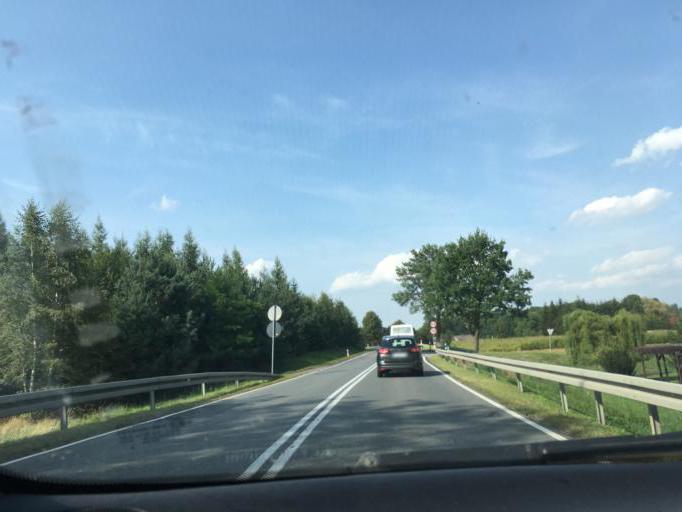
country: PL
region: Opole Voivodeship
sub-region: Powiat prudnicki
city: Laka Prudnicka
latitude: 50.3706
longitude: 17.5361
